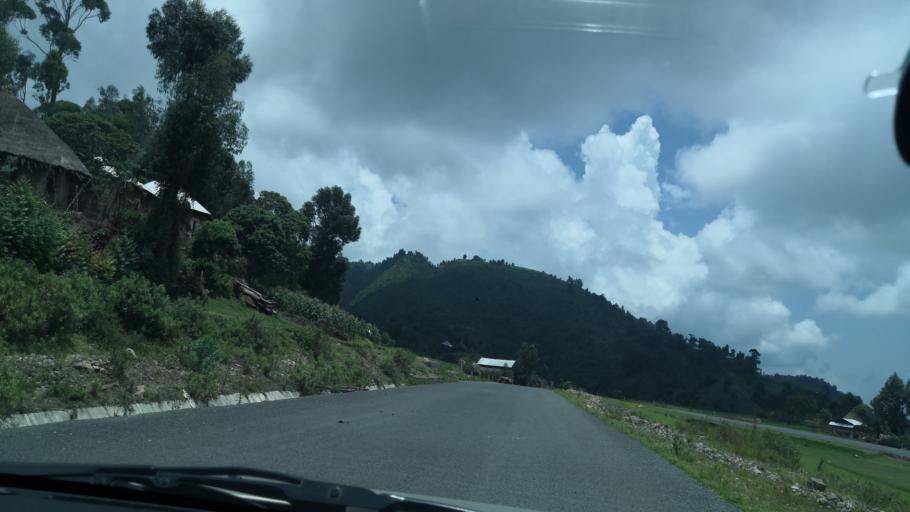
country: ET
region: Amhara
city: Abomsa
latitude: 10.3323
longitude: 39.8473
